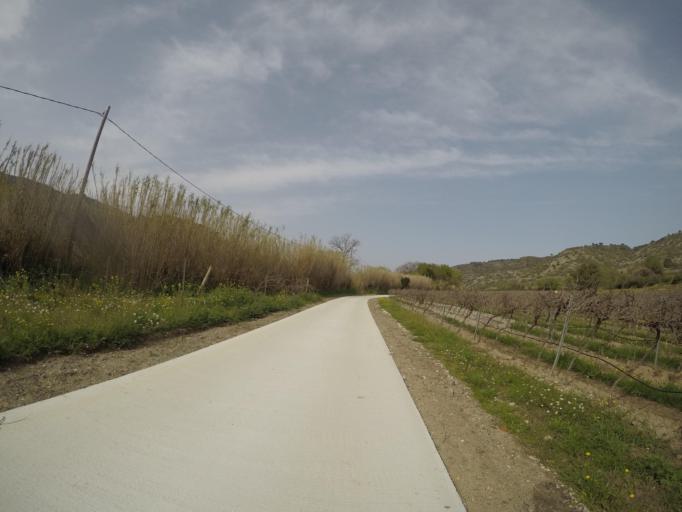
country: FR
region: Languedoc-Roussillon
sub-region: Departement des Pyrenees-Orientales
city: Estagel
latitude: 42.7774
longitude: 2.7333
